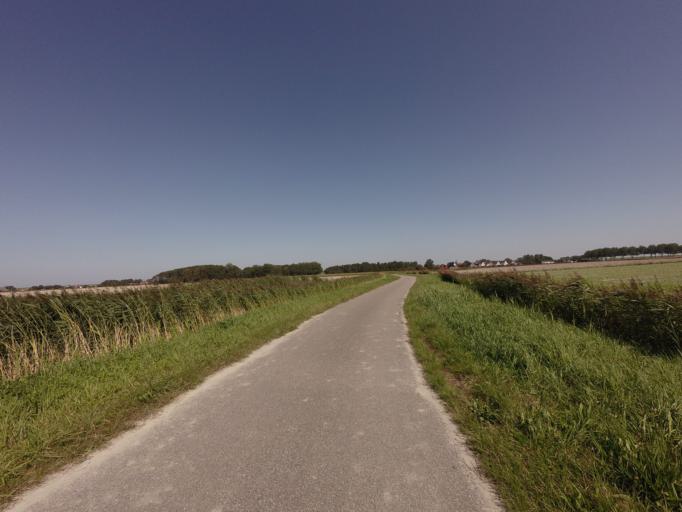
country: NL
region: Friesland
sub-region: Gemeente Dongeradeel
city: Anjum
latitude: 53.3984
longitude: 6.0775
